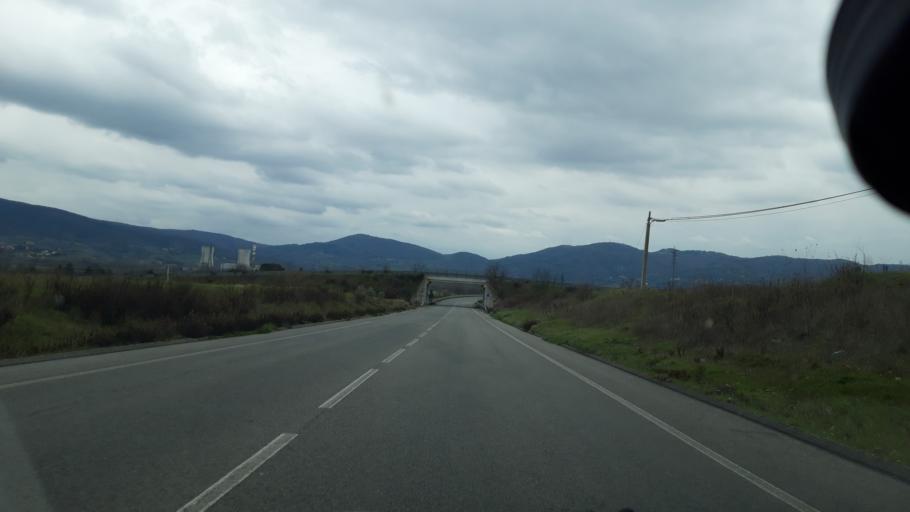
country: IT
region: Umbria
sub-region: Provincia di Perugia
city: Fontignano
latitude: 43.0141
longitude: 12.1972
